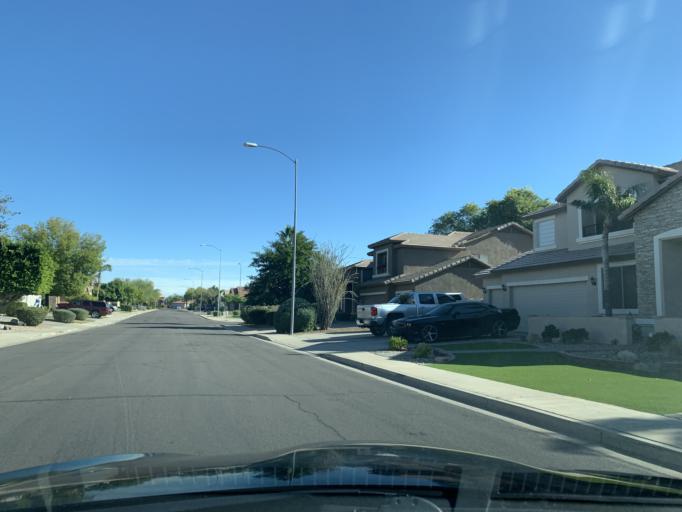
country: US
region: Arizona
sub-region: Pinal County
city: Apache Junction
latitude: 33.3827
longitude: -111.6230
